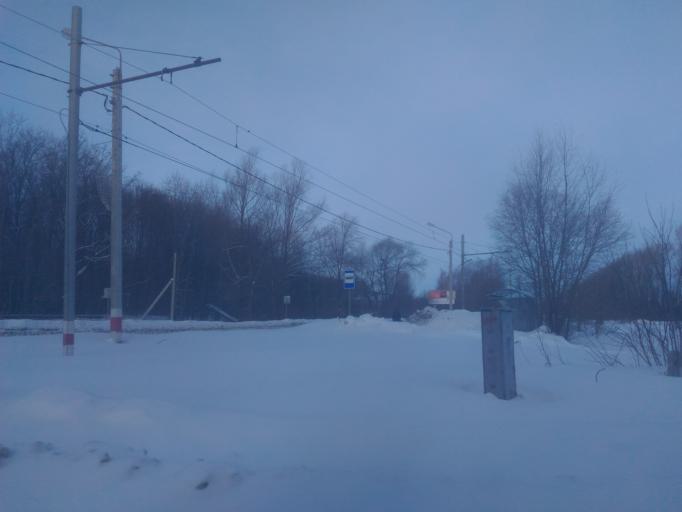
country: RU
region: Ulyanovsk
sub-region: Ulyanovskiy Rayon
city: Ulyanovsk
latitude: 54.3595
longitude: 48.3481
